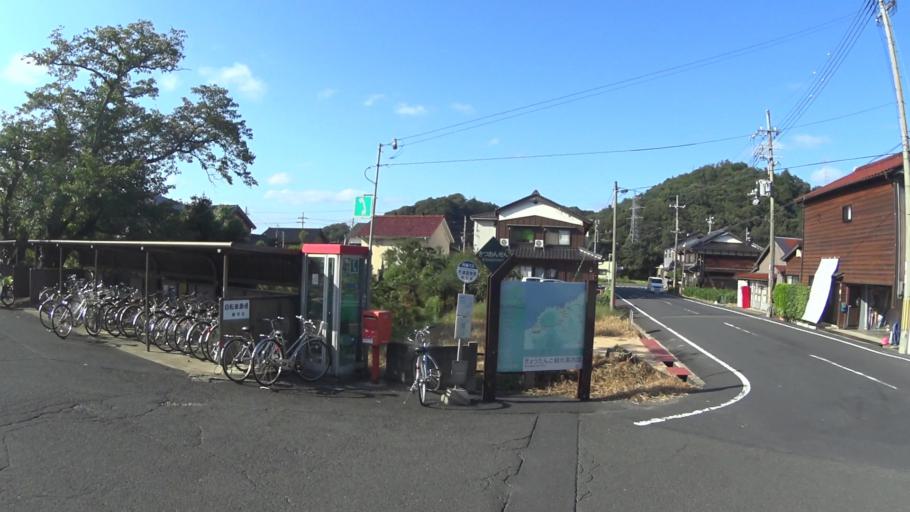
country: JP
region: Hyogo
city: Toyooka
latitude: 35.6501
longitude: 134.9725
